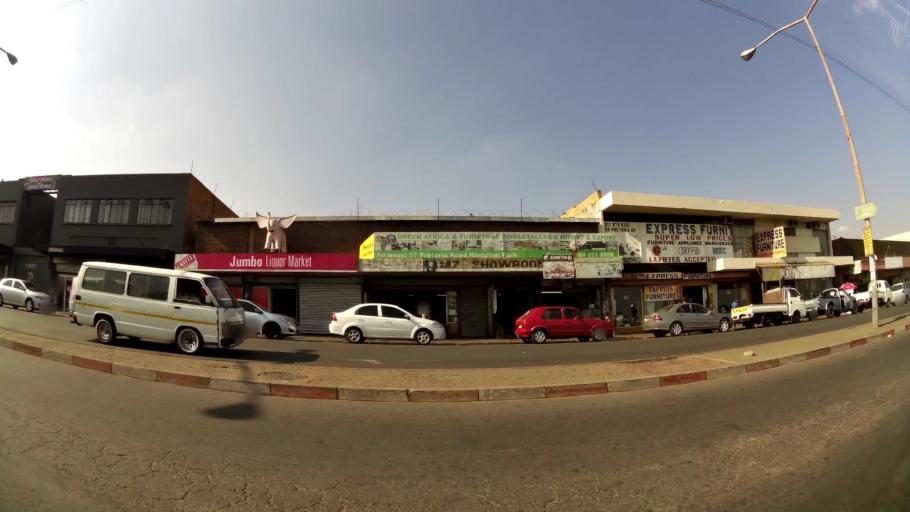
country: ZA
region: Gauteng
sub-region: City of Johannesburg Metropolitan Municipality
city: Modderfontein
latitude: -26.1091
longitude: 28.2289
